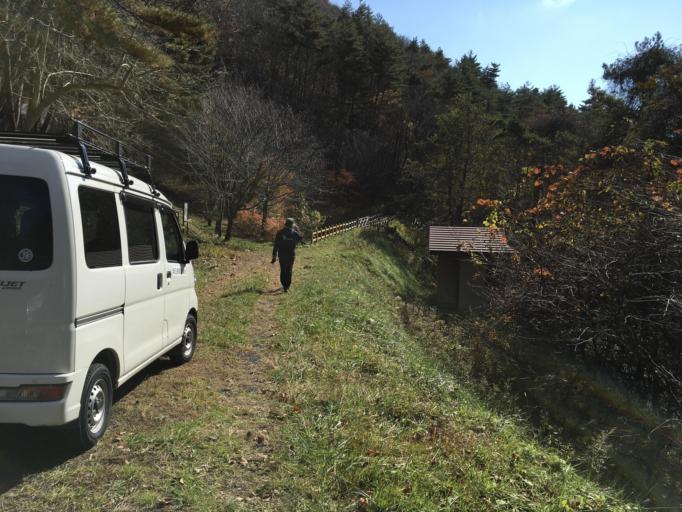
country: JP
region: Iwate
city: Ofunato
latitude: 38.9741
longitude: 141.4380
